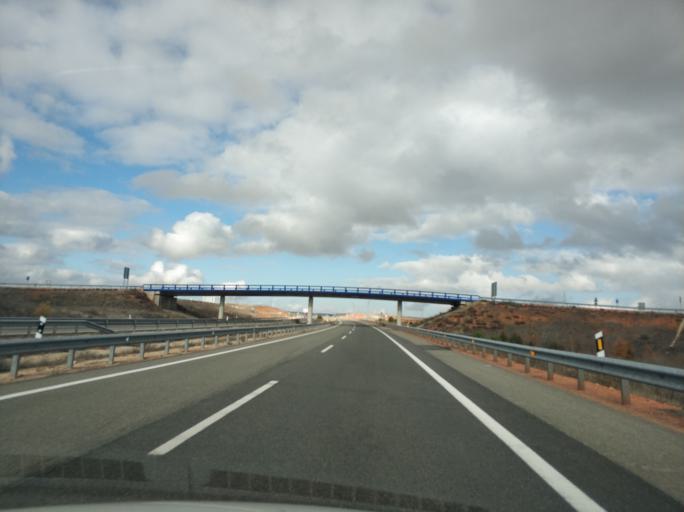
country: ES
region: Castille and Leon
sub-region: Provincia de Soria
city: Alcubilla de las Penas
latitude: 41.2599
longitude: -2.4732
